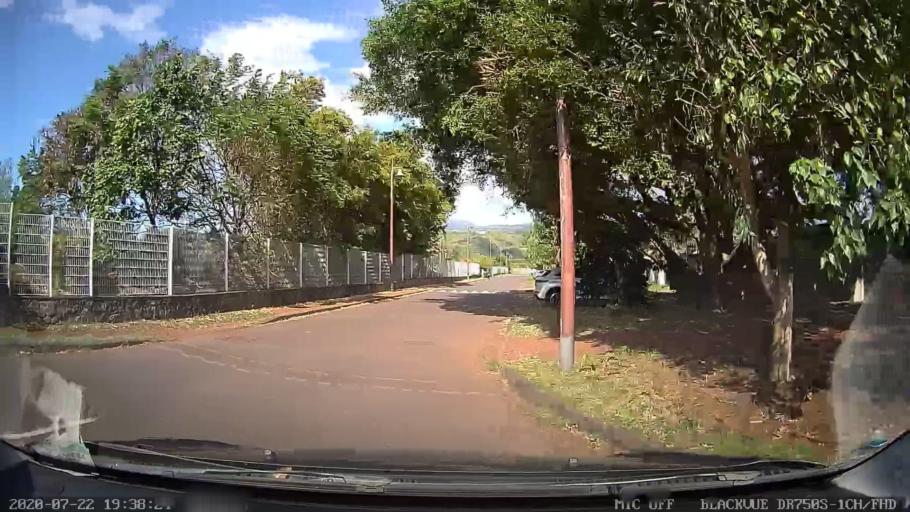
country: RE
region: Reunion
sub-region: Reunion
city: Sainte-Suzanne
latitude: -20.9120
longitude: 55.6151
